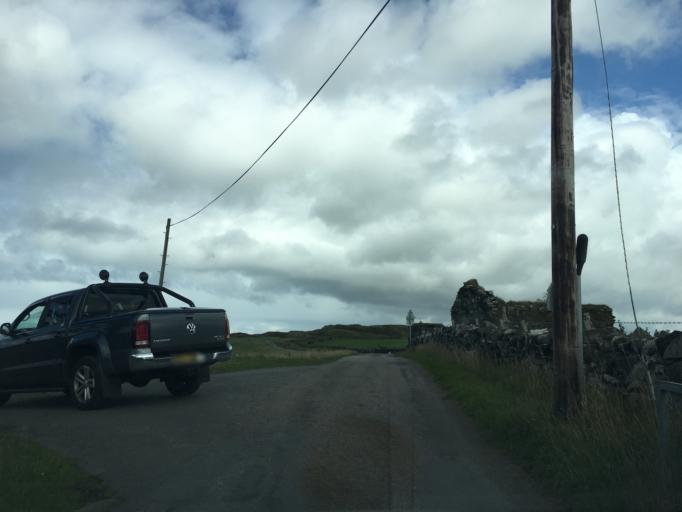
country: GB
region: Scotland
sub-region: Argyll and Bute
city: Oban
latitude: 56.2202
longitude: -5.6398
